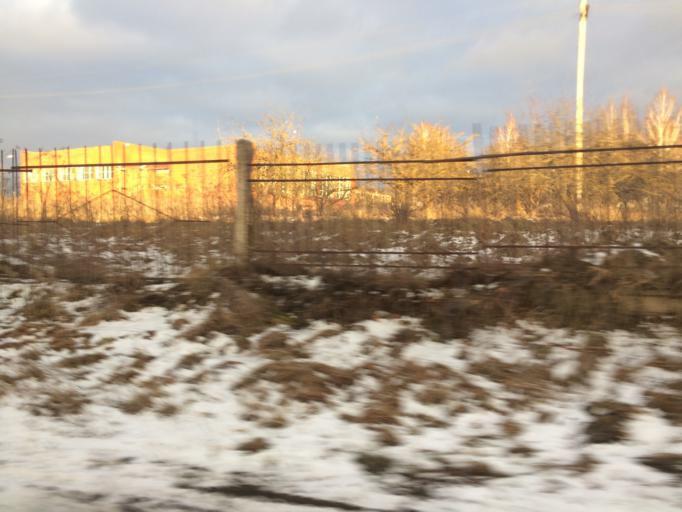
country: RU
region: Tula
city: Cherepet'
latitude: 54.1145
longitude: 36.3307
